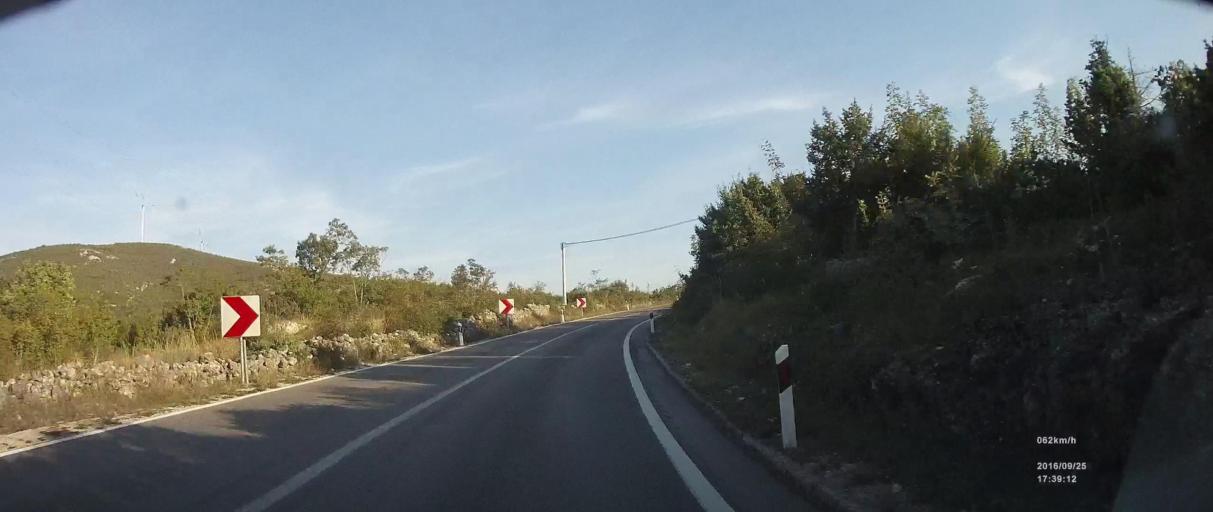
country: HR
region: Sibensko-Kniniska
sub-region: Grad Sibenik
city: Brodarica
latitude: 43.6470
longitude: 16.0609
